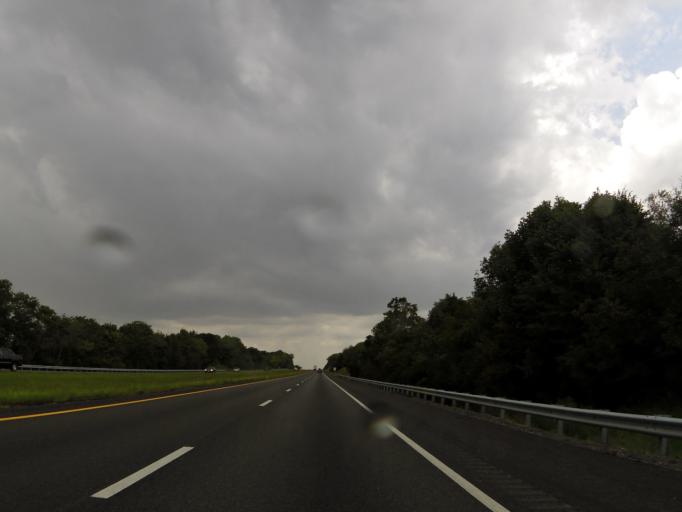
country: US
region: Tennessee
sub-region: Wilson County
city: Lebanon
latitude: 36.1926
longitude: -86.1861
